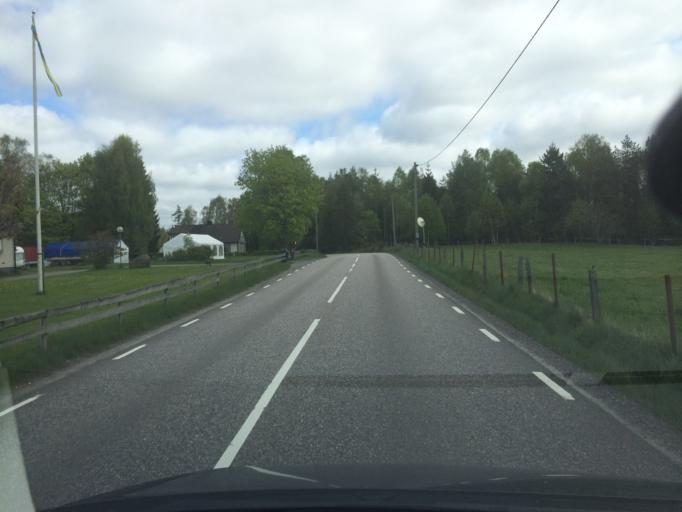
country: SE
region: Vaestra Goetaland
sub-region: Harryda Kommun
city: Hindas
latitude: 57.6980
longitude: 12.3494
